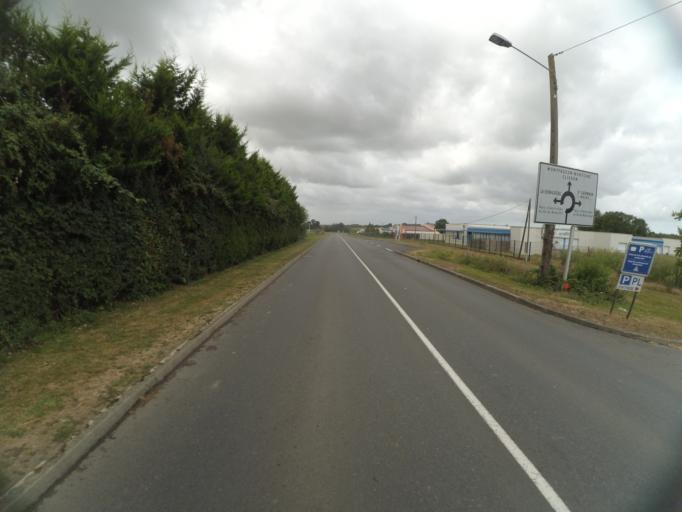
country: FR
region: Pays de la Loire
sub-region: Departement de Maine-et-Loire
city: Saint-Germain-sur-Moine
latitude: 47.1199
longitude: -1.0979
